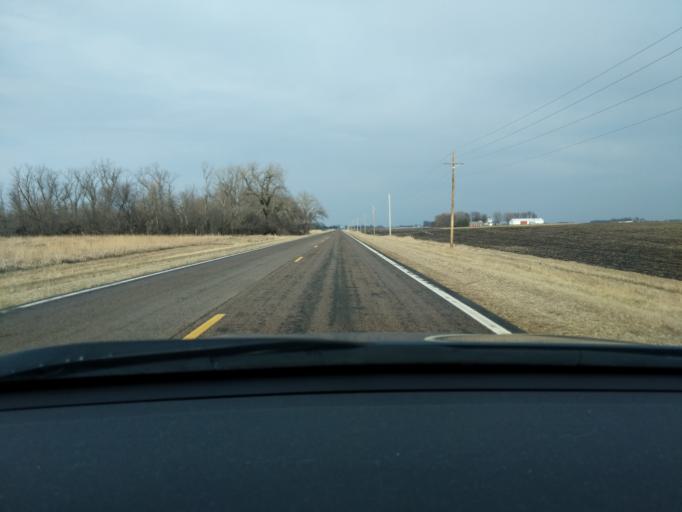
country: US
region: Minnesota
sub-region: Renville County
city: Renville
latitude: 44.7535
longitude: -95.3408
